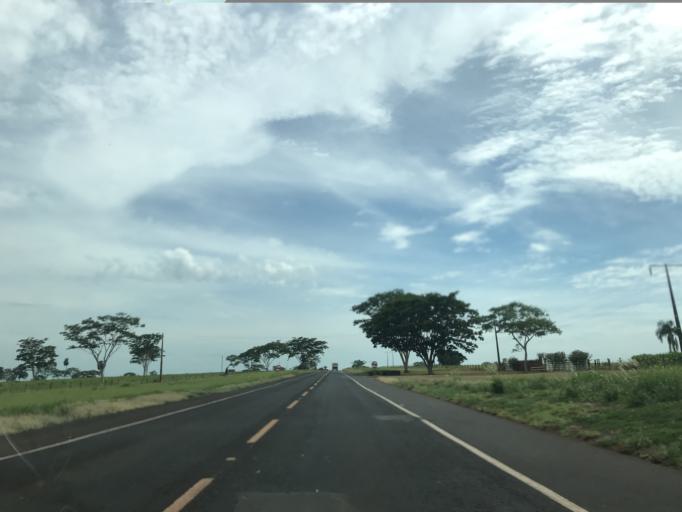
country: BR
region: Sao Paulo
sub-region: Nova Granada
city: Nova Granada
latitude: -20.3798
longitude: -49.2308
